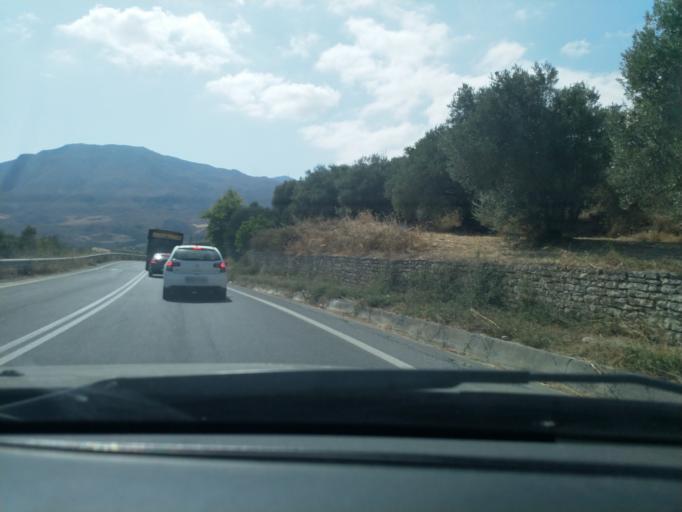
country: GR
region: Crete
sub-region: Nomos Rethymnis
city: Atsipopoulon
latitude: 35.2227
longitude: 24.4882
